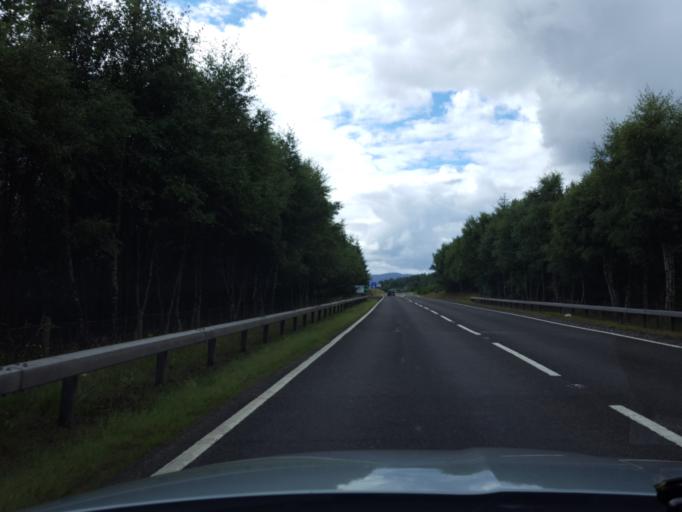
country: GB
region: Scotland
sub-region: Highland
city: Grantown on Spey
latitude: 57.3010
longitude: -3.6606
